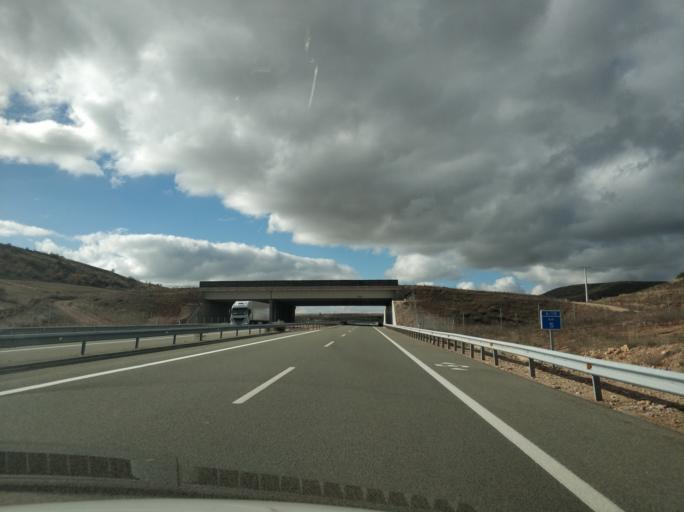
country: ES
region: Castille and Leon
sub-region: Provincia de Soria
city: Medinaceli
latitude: 41.1937
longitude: -2.4453
